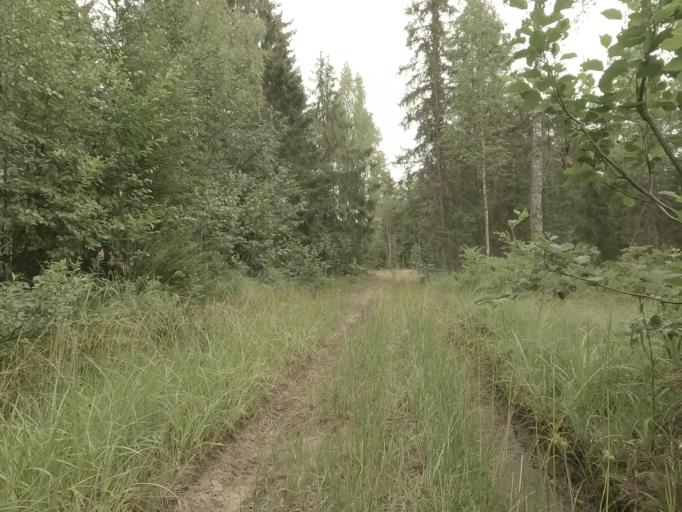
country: RU
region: Leningrad
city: Kamennogorsk
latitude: 61.0473
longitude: 29.1853
